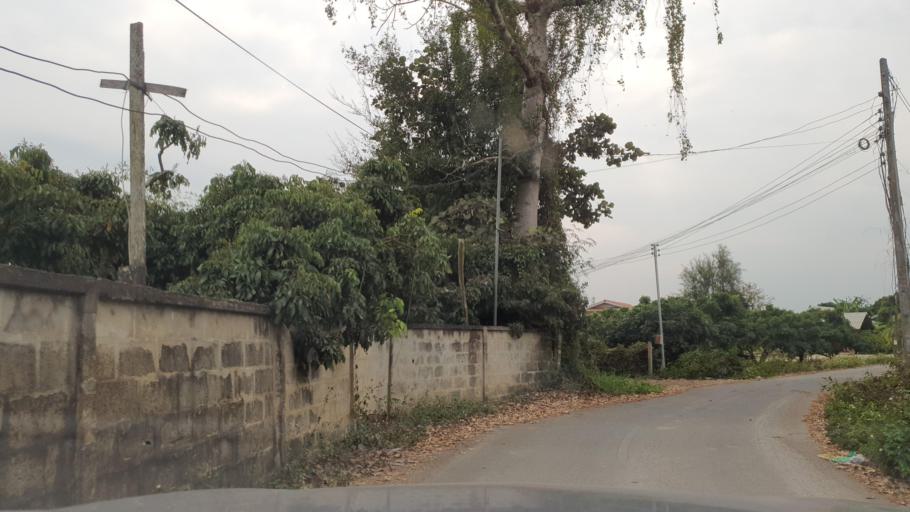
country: TH
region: Chiang Mai
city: Hang Dong
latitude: 18.6789
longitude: 98.9490
